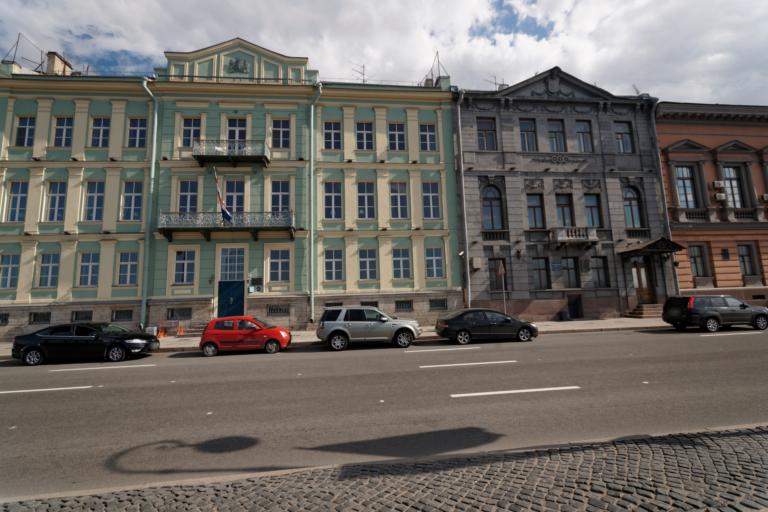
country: RU
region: St.-Petersburg
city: Saint Petersburg
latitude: 59.9352
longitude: 30.2969
